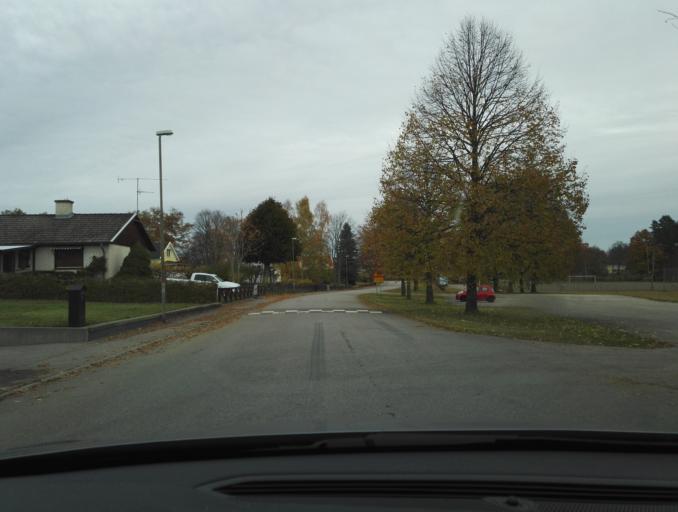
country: SE
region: Kronoberg
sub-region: Vaxjo Kommun
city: Vaexjoe
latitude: 56.9089
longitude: 14.7417
